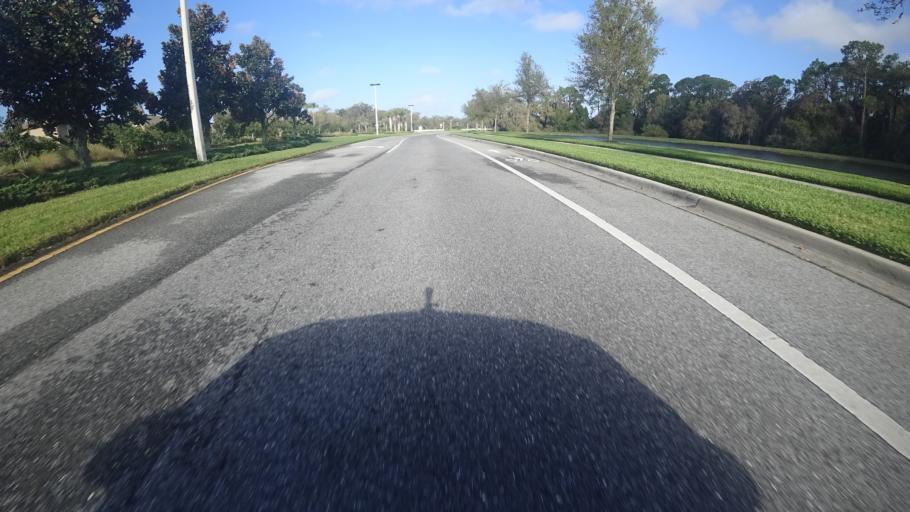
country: US
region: Florida
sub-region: Manatee County
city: Ellenton
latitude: 27.5705
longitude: -82.4663
